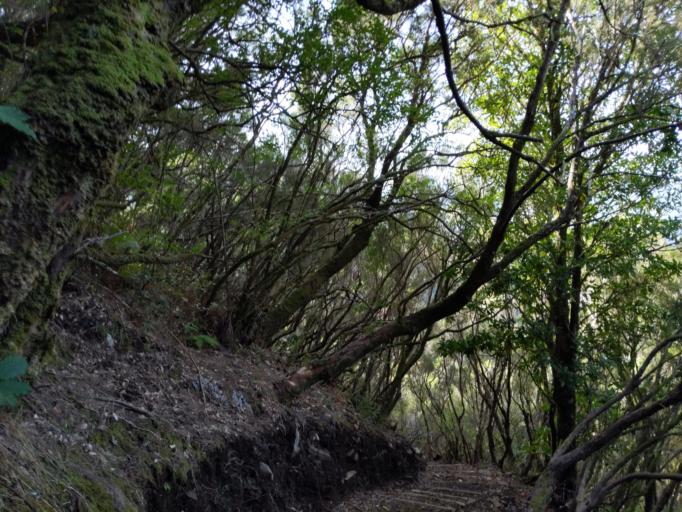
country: PT
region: Madeira
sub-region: Calheta
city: Arco da Calheta
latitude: 32.7650
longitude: -17.1255
